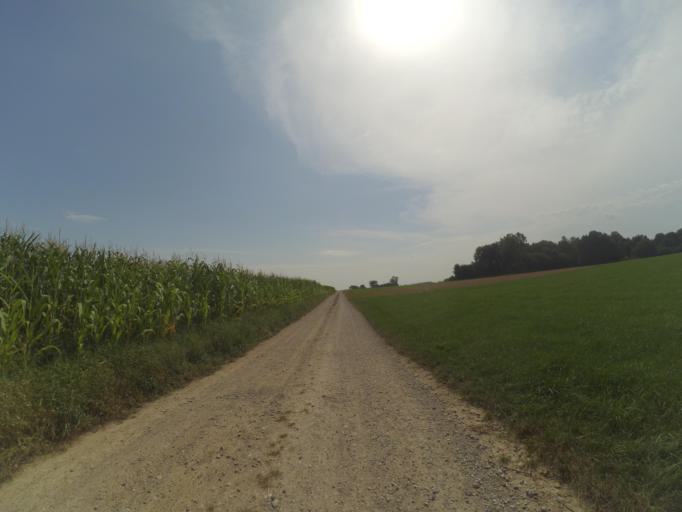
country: DE
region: Bavaria
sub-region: Swabia
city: Jengen
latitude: 48.0177
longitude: 10.7331
